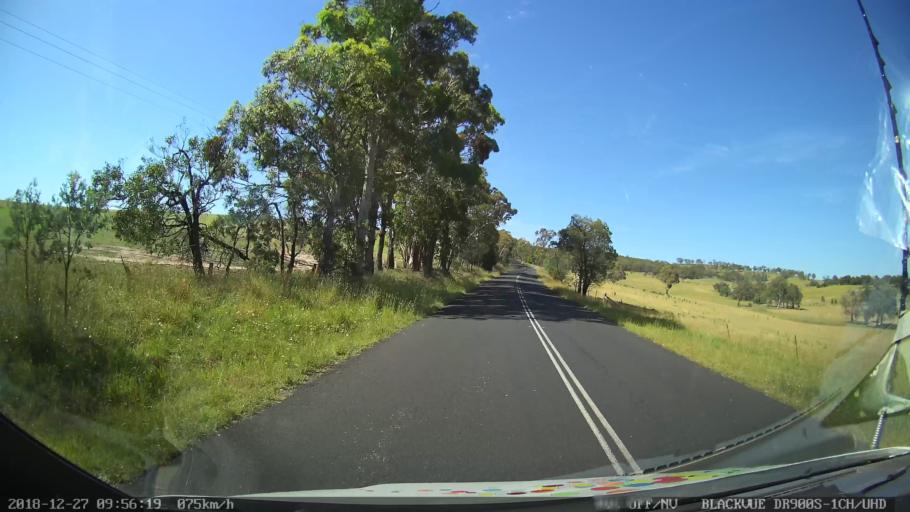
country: AU
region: New South Wales
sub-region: Lithgow
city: Portland
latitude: -33.4110
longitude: 149.9723
